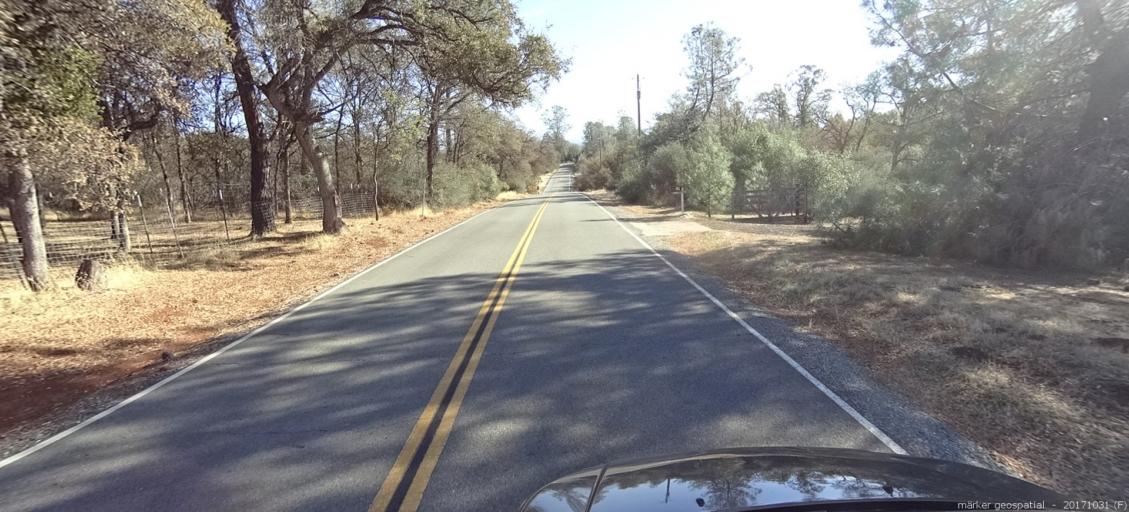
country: US
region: California
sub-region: Shasta County
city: Shingletown
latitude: 40.4463
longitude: -121.8942
